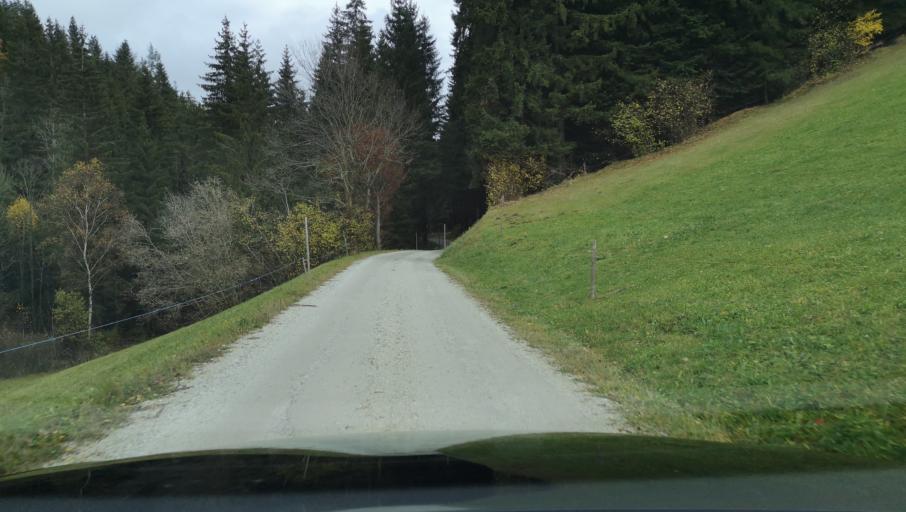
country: AT
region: Styria
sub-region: Politischer Bezirk Weiz
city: Gasen
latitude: 47.3755
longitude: 15.6110
